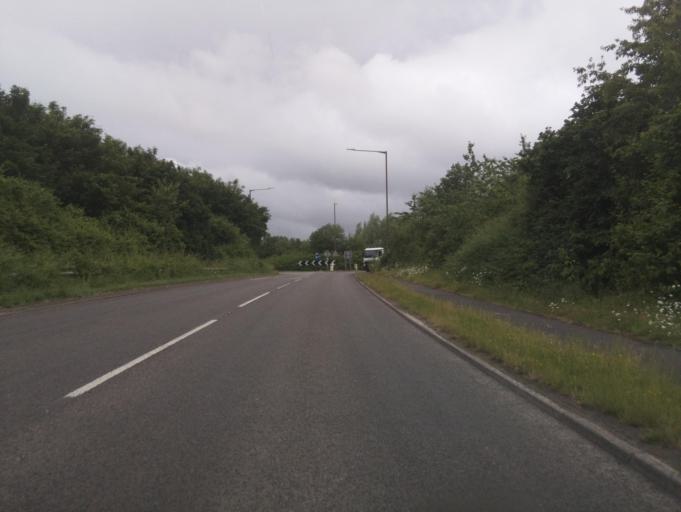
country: GB
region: England
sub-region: Derbyshire
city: Rodsley
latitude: 52.8794
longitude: -1.7003
